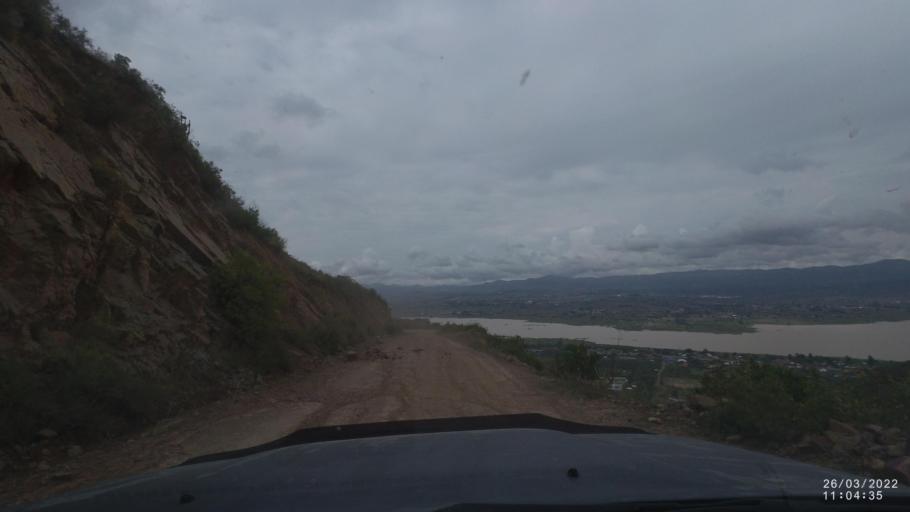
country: BO
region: Cochabamba
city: Tarata
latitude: -17.5303
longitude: -66.0258
